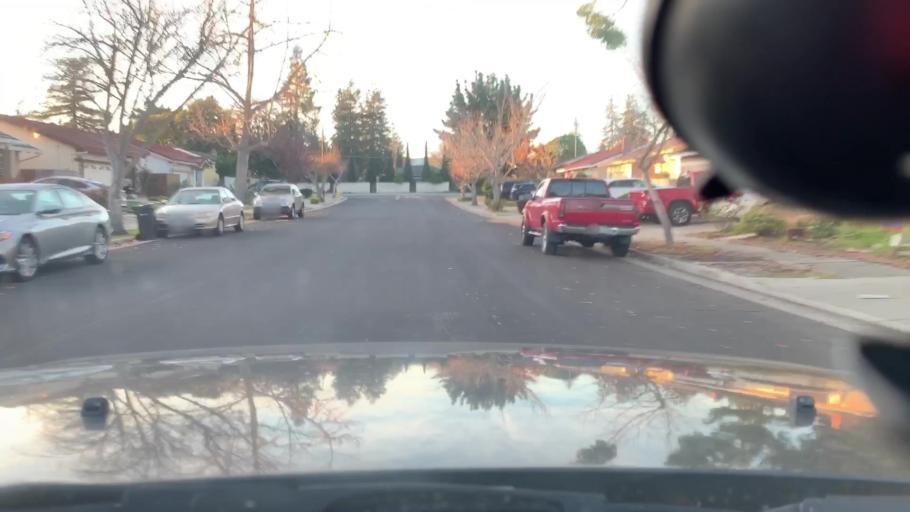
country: US
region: California
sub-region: Santa Clara County
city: Campbell
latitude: 37.2878
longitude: -121.9639
